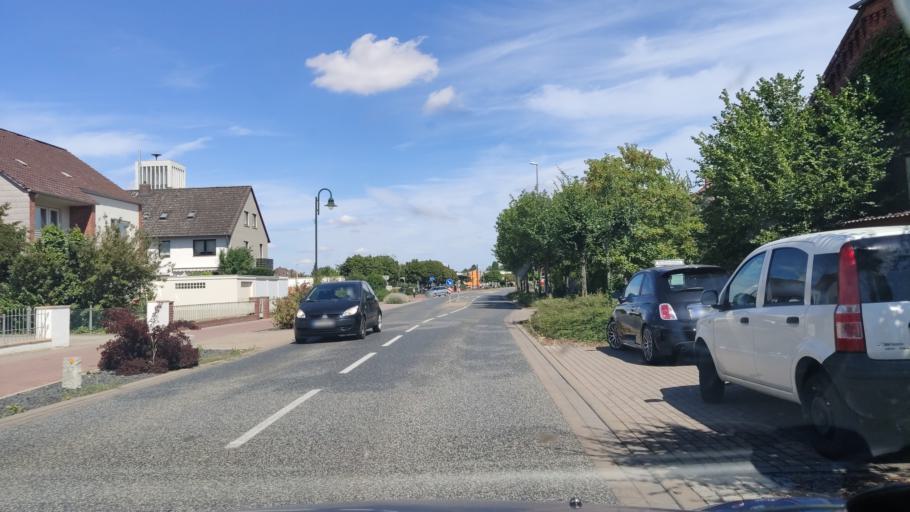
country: DE
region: Lower Saxony
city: Ronnenberg
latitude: 52.3436
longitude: 9.6638
